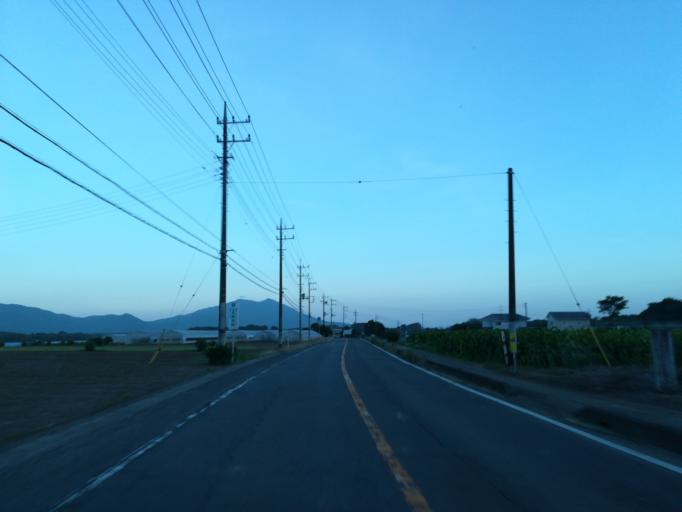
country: JP
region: Ibaraki
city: Iwase
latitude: 36.3403
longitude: 140.0748
